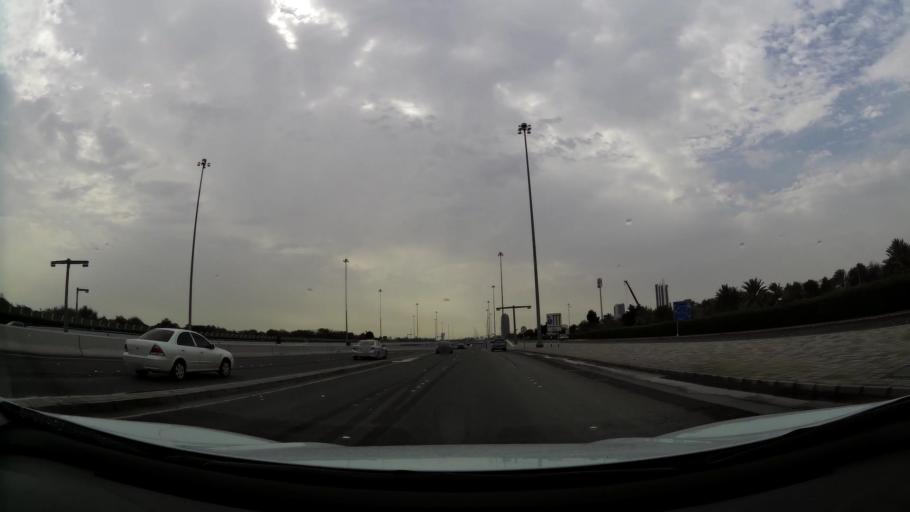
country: AE
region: Abu Dhabi
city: Abu Dhabi
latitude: 24.4761
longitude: 54.3895
